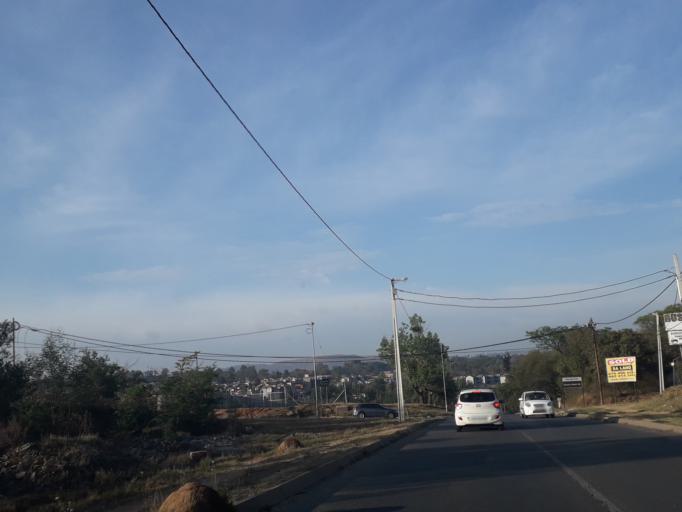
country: ZA
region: Gauteng
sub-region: West Rand District Municipality
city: Muldersdriseloop
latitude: -26.0806
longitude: 27.9068
